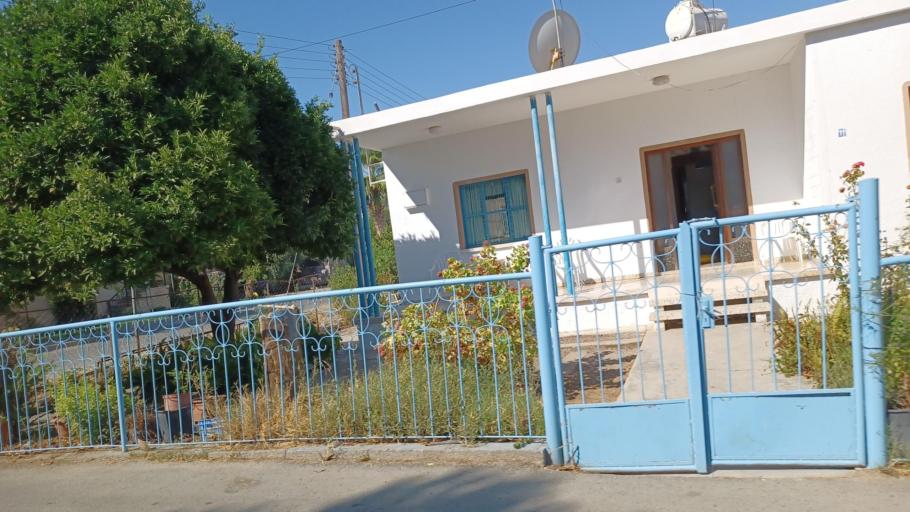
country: CY
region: Pafos
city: Polis
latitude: 35.0379
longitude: 32.4276
